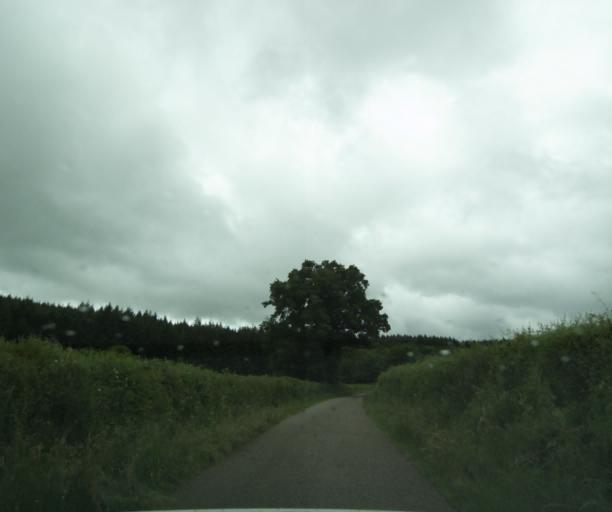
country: FR
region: Bourgogne
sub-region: Departement de Saone-et-Loire
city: Matour
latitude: 46.4327
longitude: 4.4446
